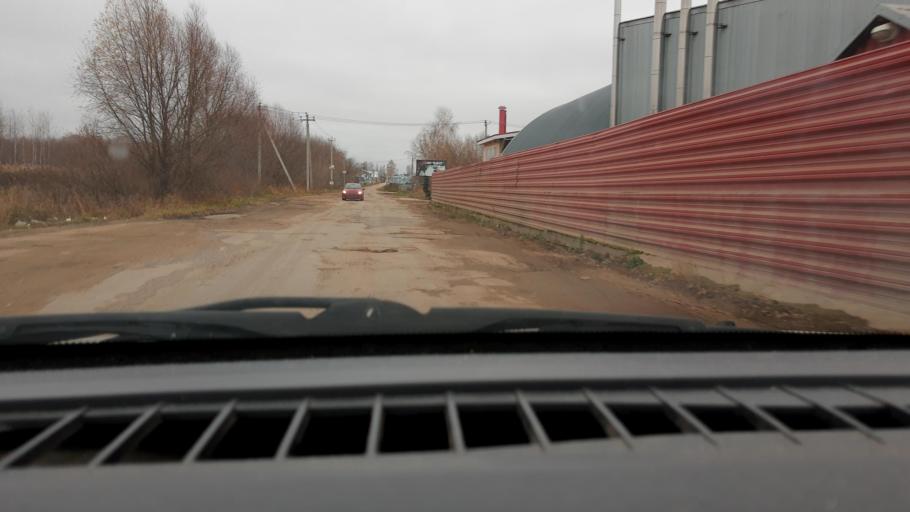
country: RU
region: Nizjnij Novgorod
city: Kstovo
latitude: 56.1960
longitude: 44.1492
